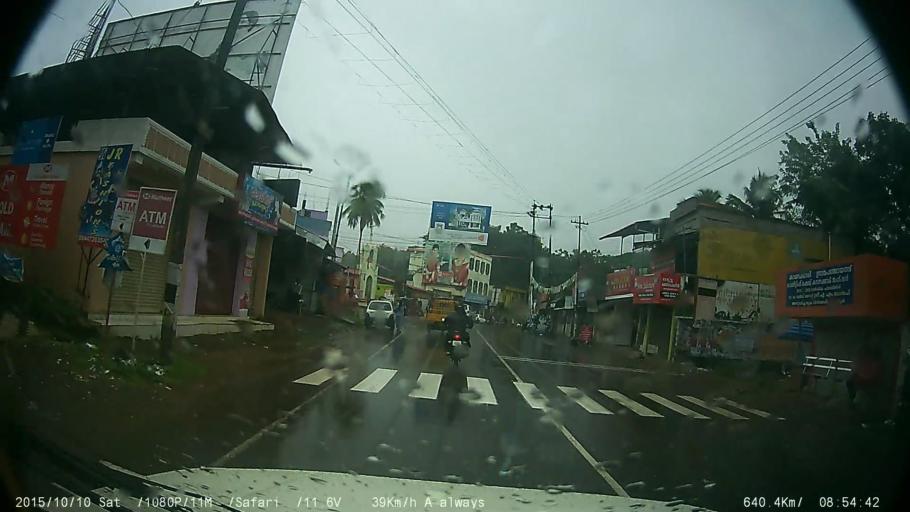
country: IN
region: Kerala
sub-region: Kottayam
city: Palackattumala
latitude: 9.7025
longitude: 76.5471
